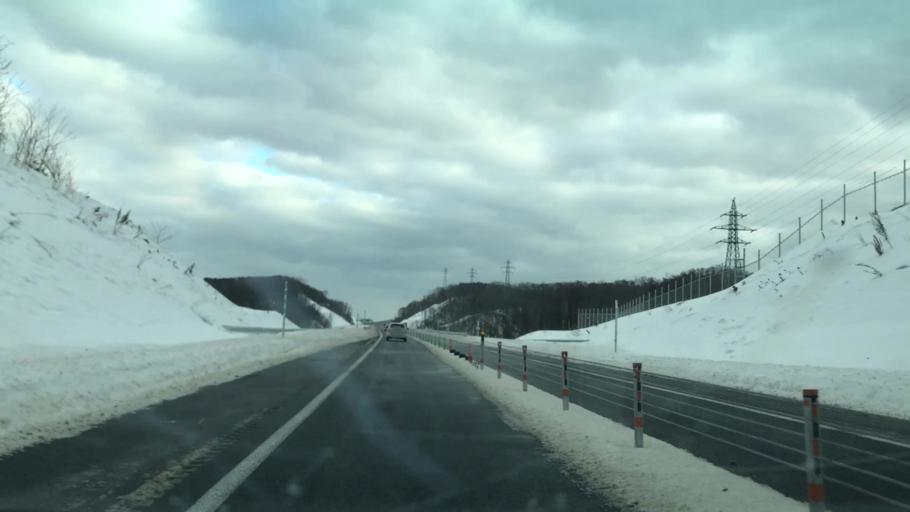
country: JP
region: Hokkaido
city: Otaru
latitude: 43.1958
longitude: 140.8968
